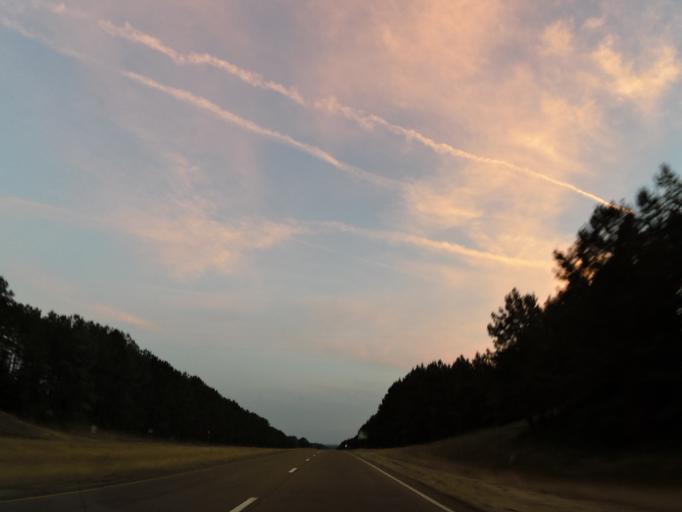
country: US
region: Mississippi
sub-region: Lauderdale County
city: Meridian Station
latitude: 32.5790
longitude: -88.5029
